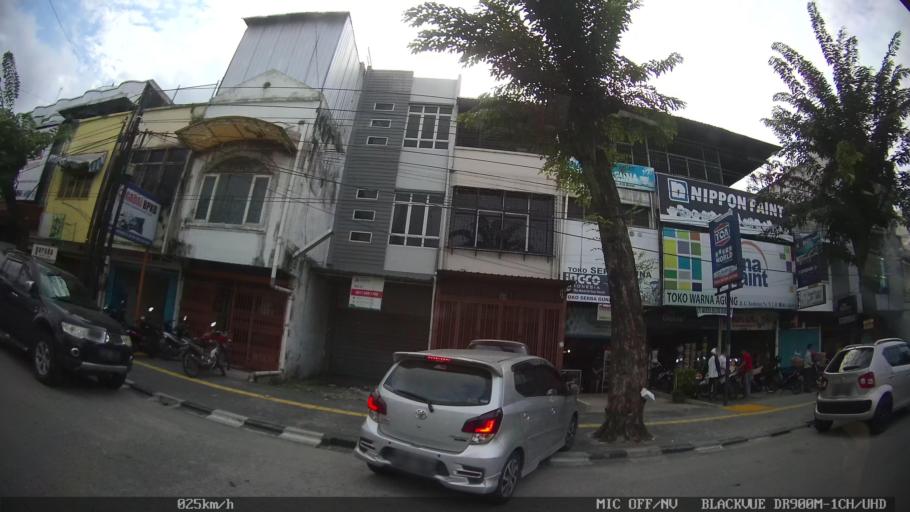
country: ID
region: North Sumatra
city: Medan
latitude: 3.6126
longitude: 98.6802
